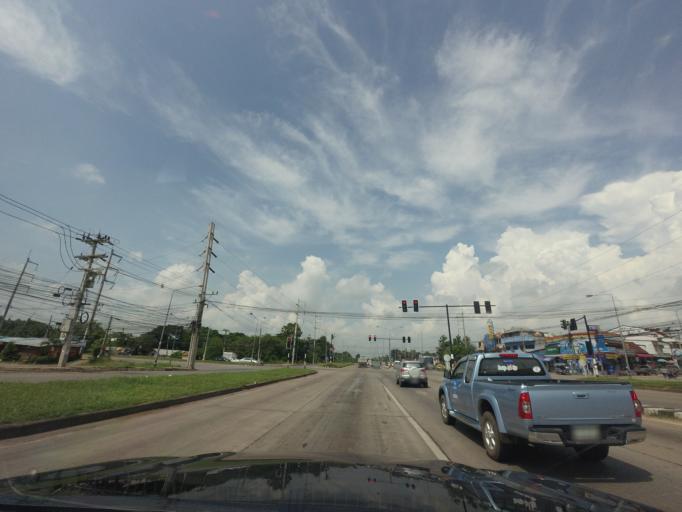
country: TH
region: Khon Kaen
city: Ban Fang
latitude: 16.4499
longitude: 102.7153
